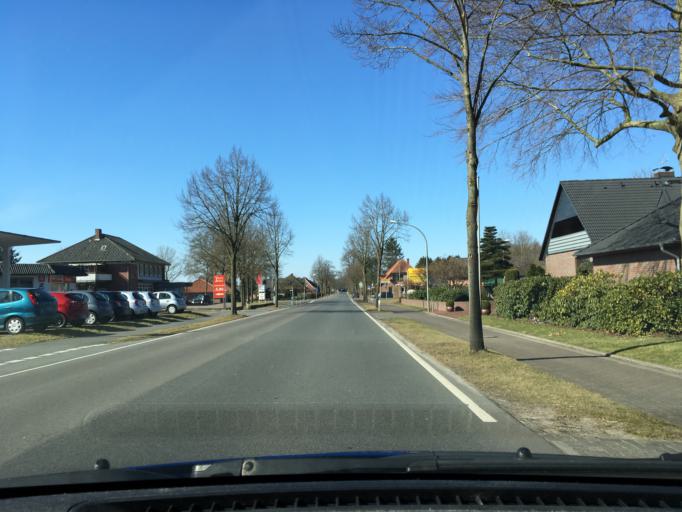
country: DE
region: Lower Saxony
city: Brockel
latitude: 53.0946
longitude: 9.5226
